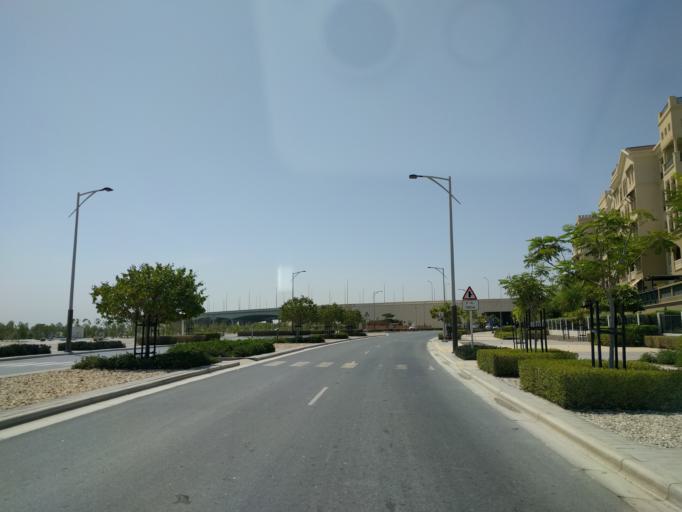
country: AE
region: Abu Dhabi
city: Abu Dhabi
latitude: 24.5510
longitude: 54.4537
